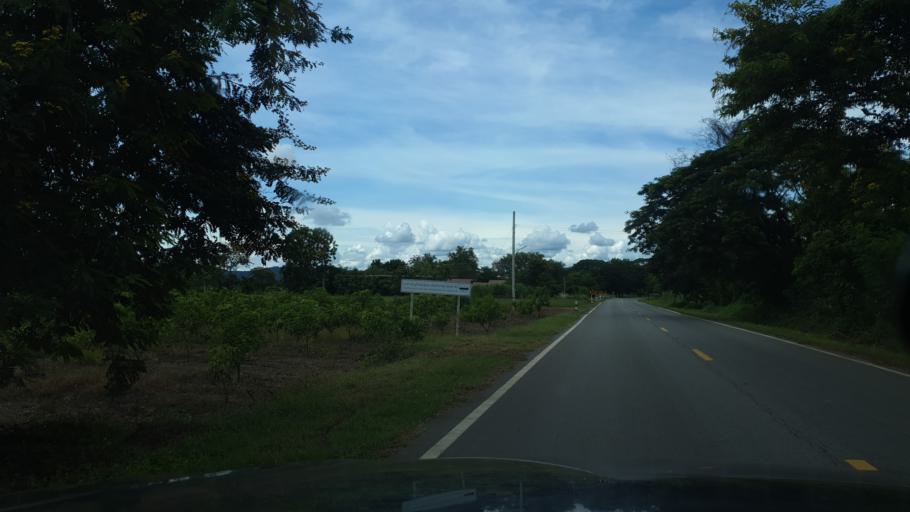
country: TH
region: Sukhothai
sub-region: Amphoe Si Satchanalai
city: Si Satchanalai
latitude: 17.4741
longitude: 99.7542
